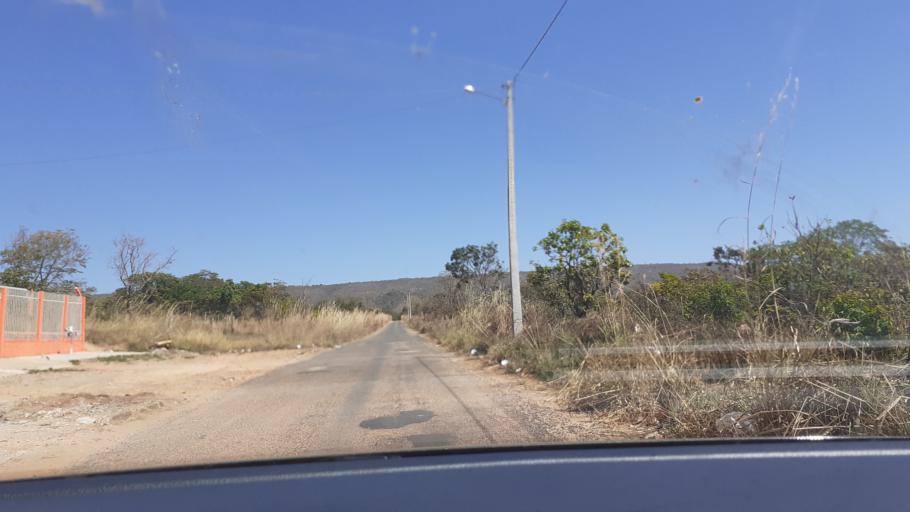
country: BR
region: Goias
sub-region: Caldas Novas
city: Caldas Novas
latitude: -17.7408
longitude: -48.6550
